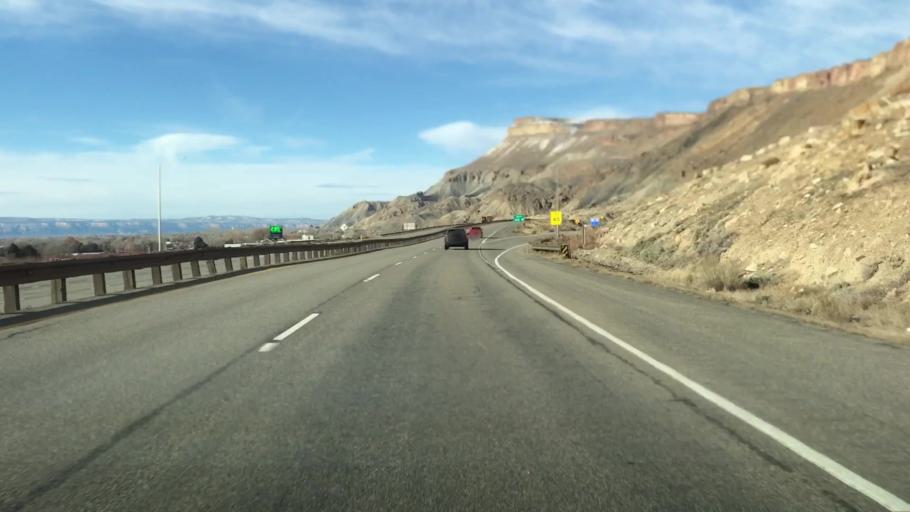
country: US
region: Colorado
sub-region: Mesa County
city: Palisade
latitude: 39.1169
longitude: -108.3540
